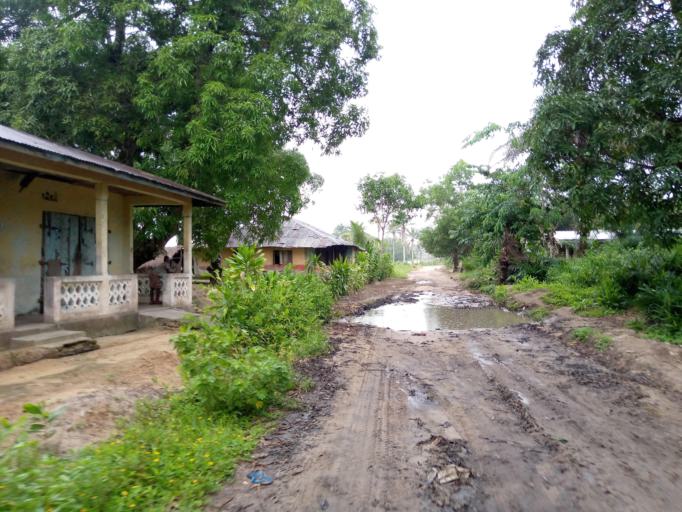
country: SL
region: Southern Province
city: Bonthe
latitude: 7.5276
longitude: -12.5107
